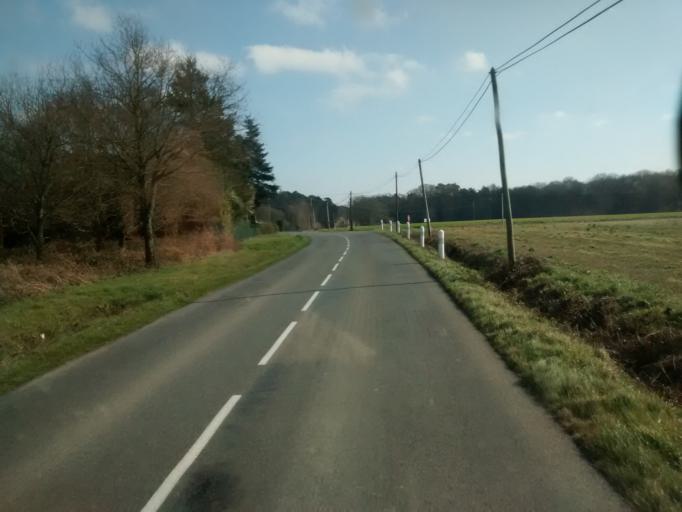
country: FR
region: Brittany
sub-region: Departement d'Ille-et-Vilaine
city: Paimpont
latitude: 48.0395
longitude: -2.1825
